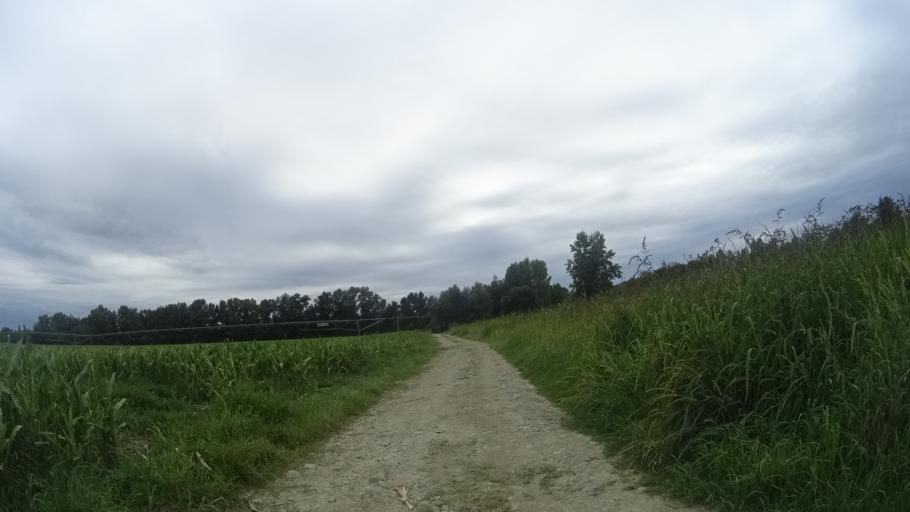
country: FR
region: Aquitaine
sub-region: Departement des Pyrenees-Atlantiques
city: Orthez
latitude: 43.4654
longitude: -0.7210
